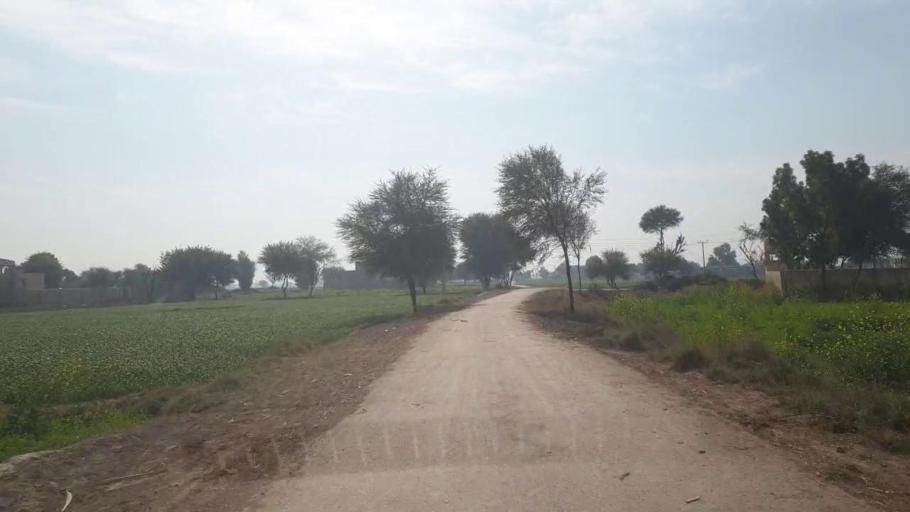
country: PK
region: Sindh
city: Nawabshah
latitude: 26.1613
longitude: 68.5021
